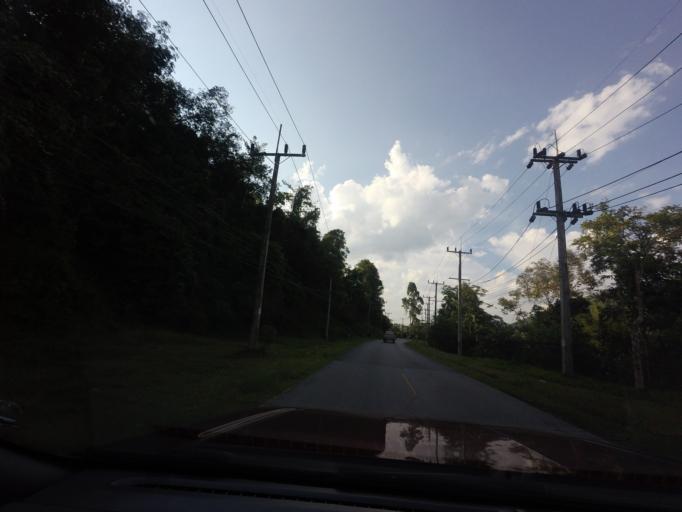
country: TH
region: Yala
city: Than To
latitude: 6.1760
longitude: 101.2656
